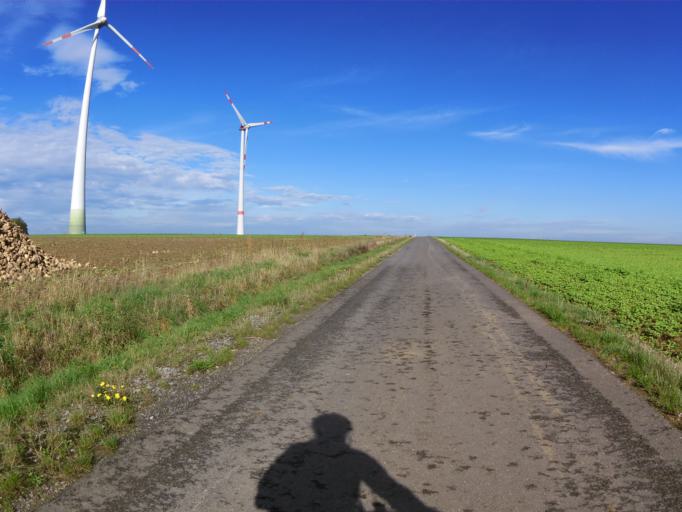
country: DE
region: Bavaria
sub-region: Regierungsbezirk Unterfranken
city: Sommerhausen
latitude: 49.7158
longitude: 10.0462
